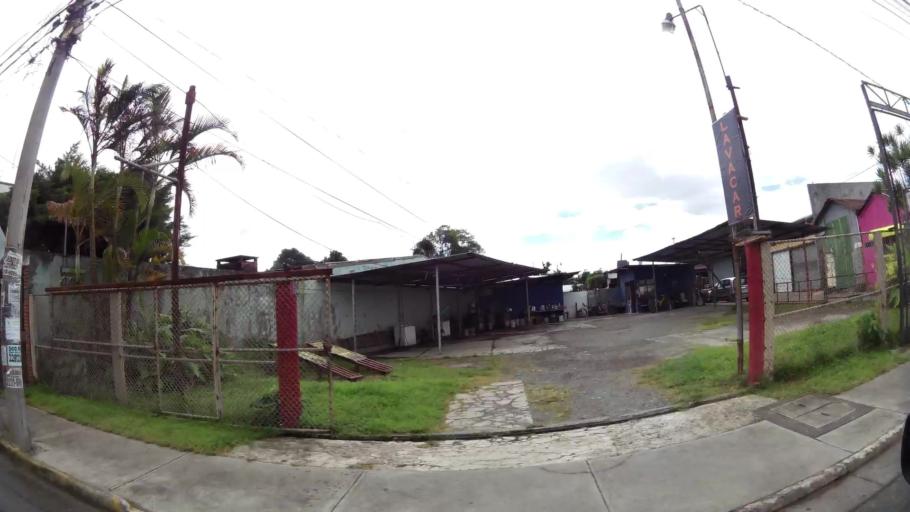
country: CR
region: San Jose
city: San Vicente
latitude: 9.9628
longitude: -84.0449
